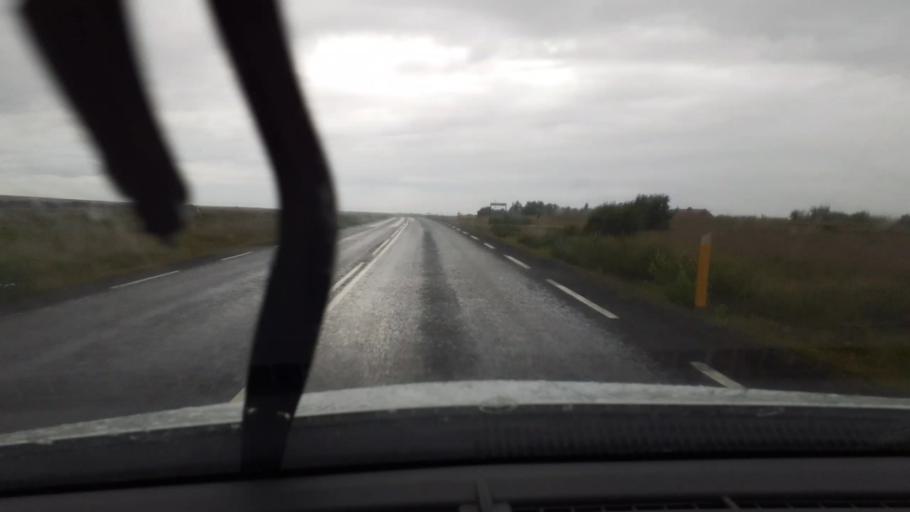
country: IS
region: West
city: Akranes
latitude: 64.3650
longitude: -21.9377
